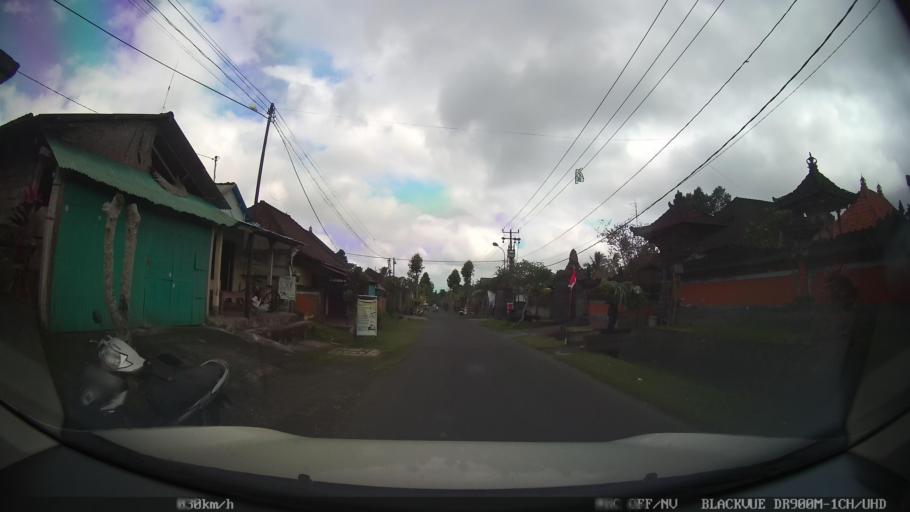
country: ID
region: Bali
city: Banjar Susut Kaja
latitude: -8.4368
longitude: 115.3220
